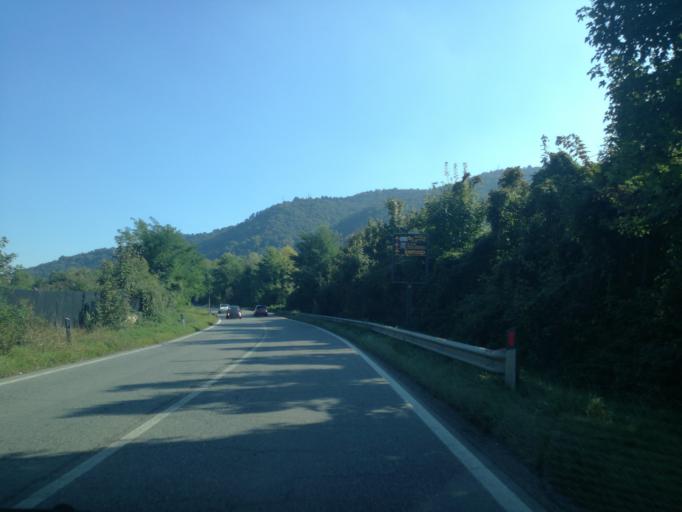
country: IT
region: Lombardy
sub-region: Provincia di Bergamo
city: Caprino
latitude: 45.7354
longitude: 9.4868
